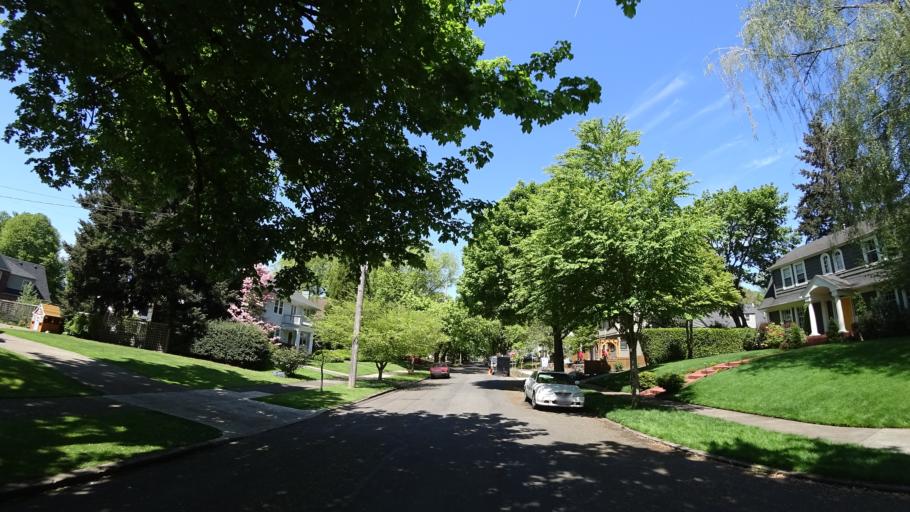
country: US
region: Oregon
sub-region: Clackamas County
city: Milwaukie
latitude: 45.4764
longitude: -122.6282
